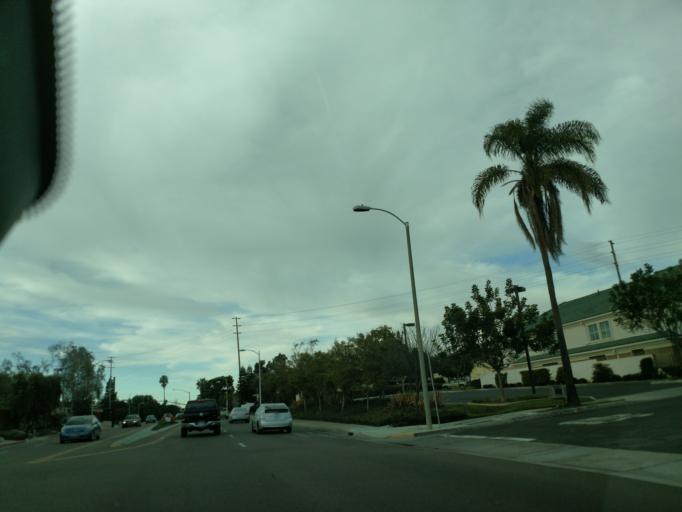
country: US
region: California
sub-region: San Diego County
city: Coronado
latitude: 32.7379
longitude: -117.2309
